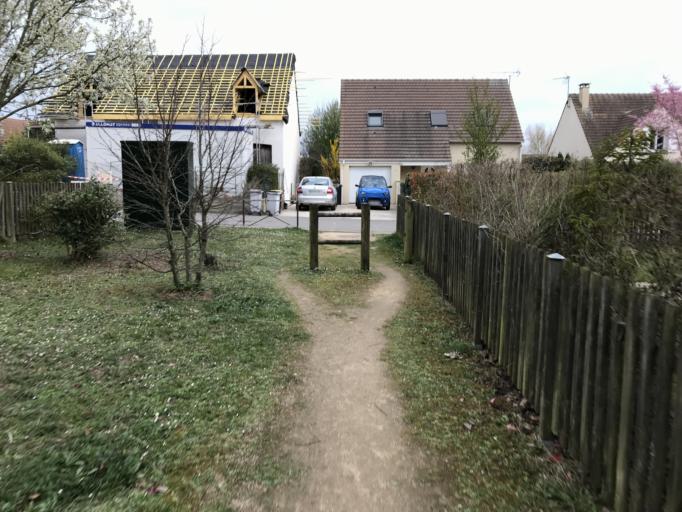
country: FR
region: Ile-de-France
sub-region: Departement de l'Essonne
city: Gometz-la-Ville
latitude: 48.6707
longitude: 2.1203
